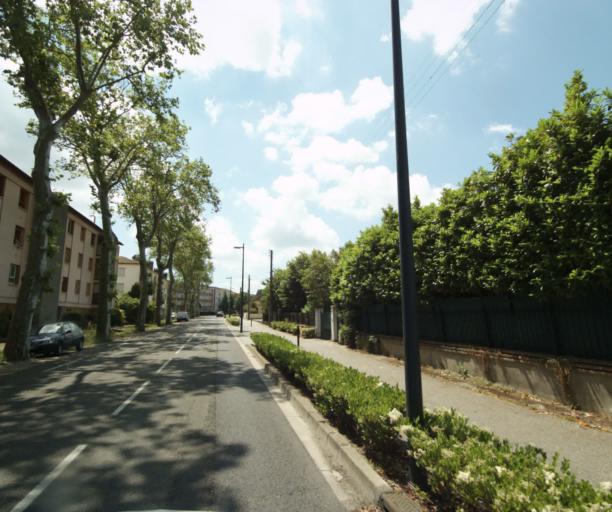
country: FR
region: Midi-Pyrenees
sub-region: Departement du Tarn-et-Garonne
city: Montauban
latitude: 44.0288
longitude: 1.3578
